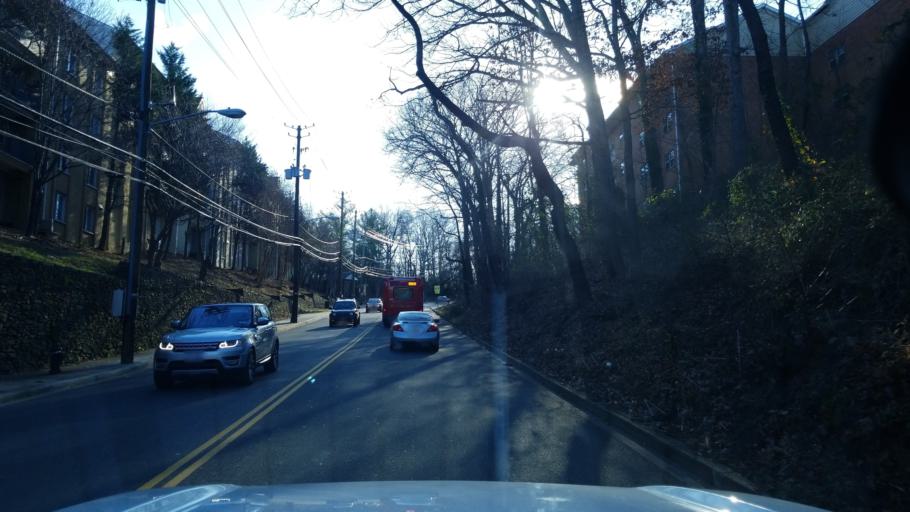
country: US
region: Maryland
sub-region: Prince George's County
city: Hillcrest Heights
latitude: 38.8524
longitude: -76.9822
